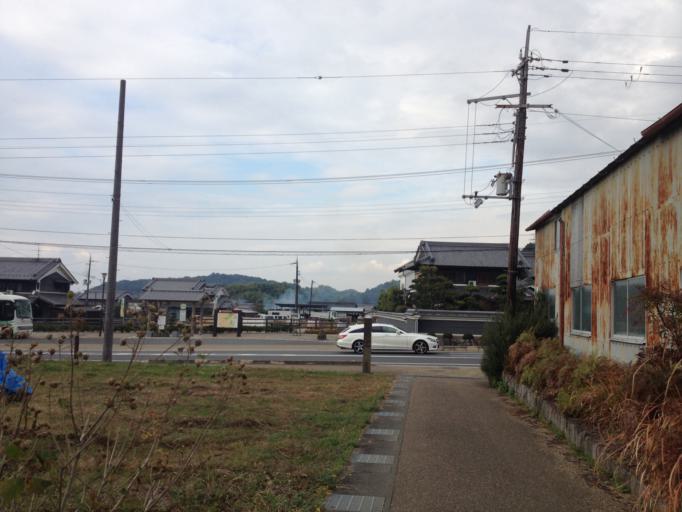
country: JP
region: Nara
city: Sakurai
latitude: 34.4832
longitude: 135.8230
